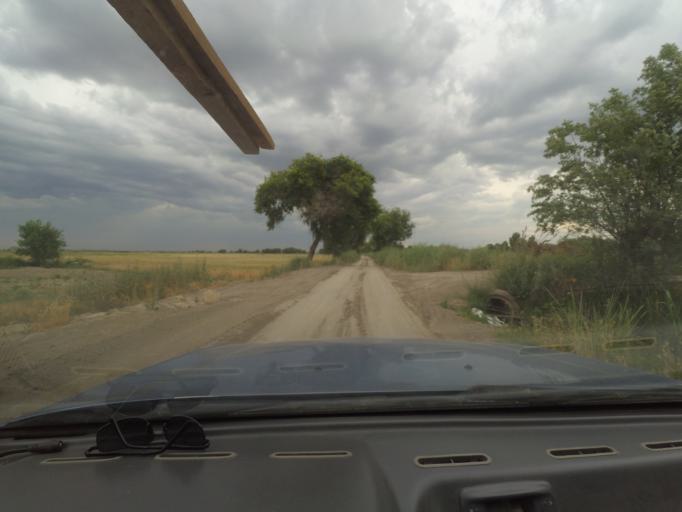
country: TJ
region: Viloyati Sughd
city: Buston
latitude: 40.5495
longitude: 69.0779
